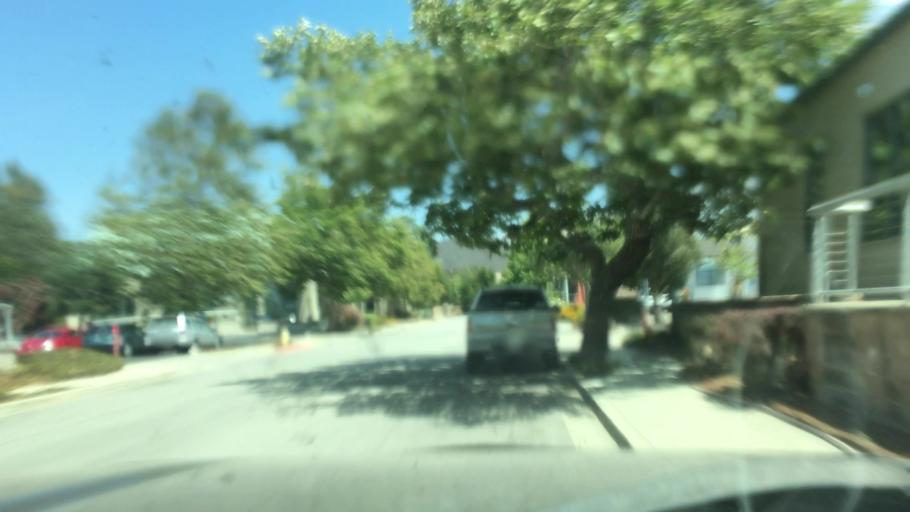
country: US
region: California
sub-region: San Luis Obispo County
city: San Luis Obispo
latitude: 35.2442
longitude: -120.6468
